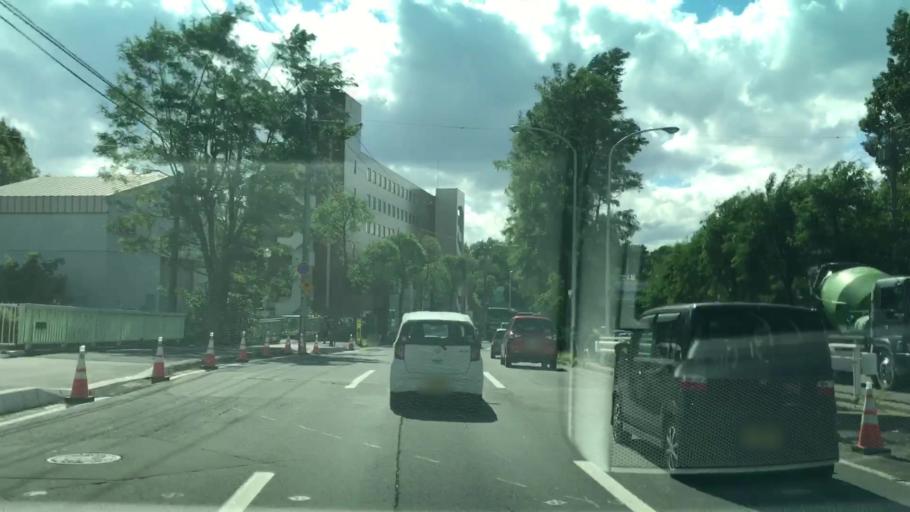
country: JP
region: Hokkaido
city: Sapporo
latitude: 43.0274
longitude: 141.4519
